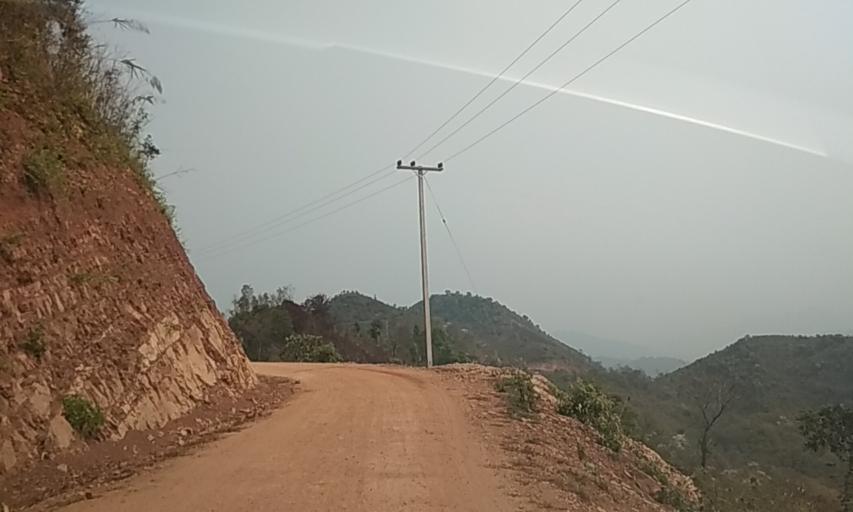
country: VN
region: Huyen Dien Bien
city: Dien Bien Phu
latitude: 21.5037
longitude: 102.7928
